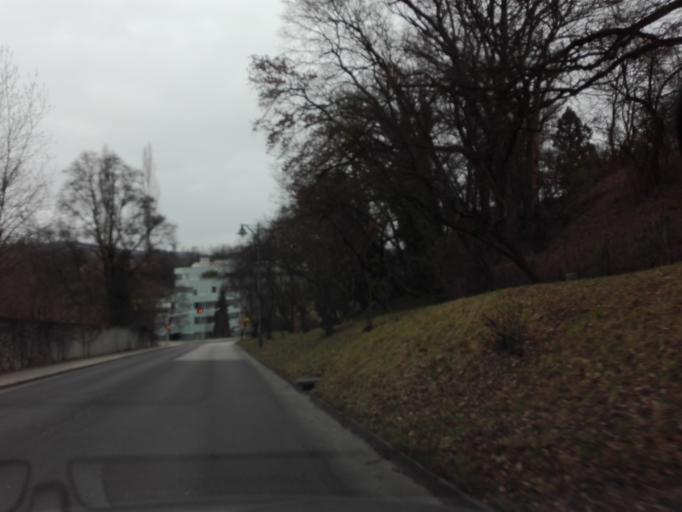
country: AT
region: Upper Austria
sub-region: Linz Stadt
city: Linz
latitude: 48.2968
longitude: 14.2752
